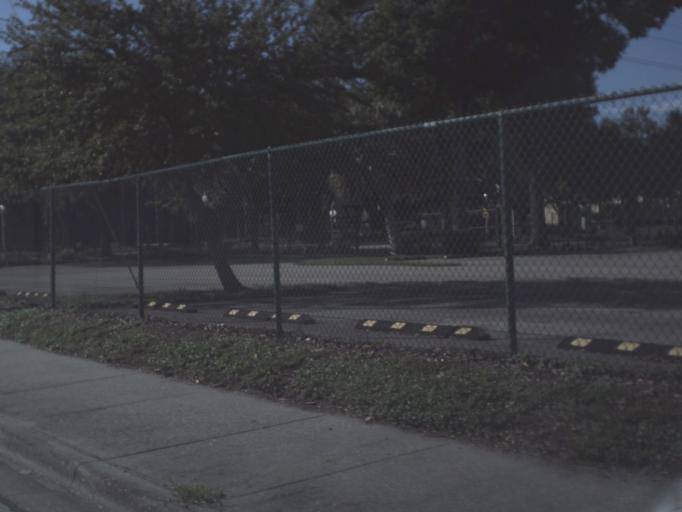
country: US
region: Florida
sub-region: Lee County
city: North Fort Myers
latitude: 26.6426
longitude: -81.8634
